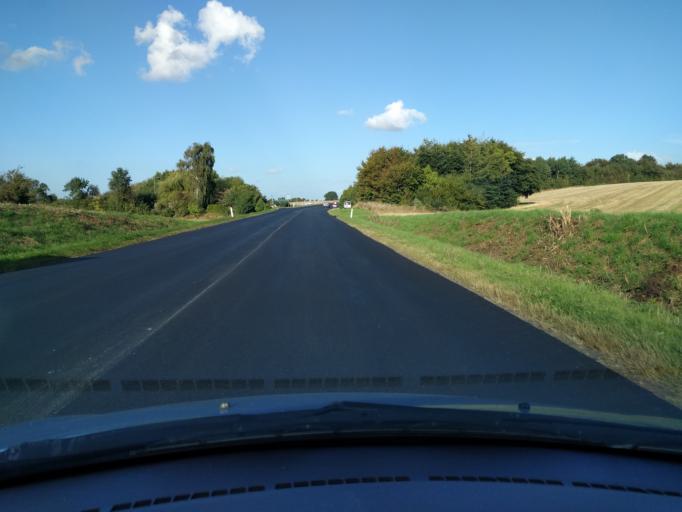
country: DK
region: South Denmark
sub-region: Assens Kommune
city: Glamsbjerg
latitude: 55.2732
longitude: 10.1397
